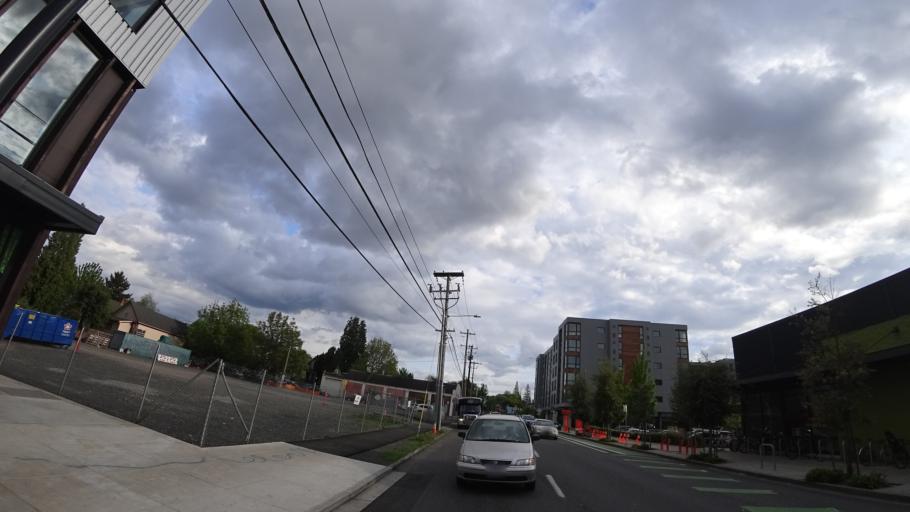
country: US
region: Oregon
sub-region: Multnomah County
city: Portland
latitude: 45.5480
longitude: -122.6666
